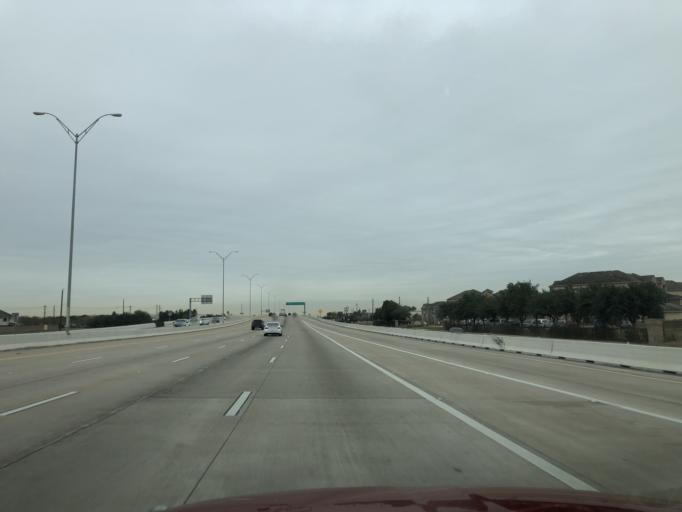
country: US
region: Texas
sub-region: Fort Bend County
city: Missouri City
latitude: 29.6343
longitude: -95.5271
